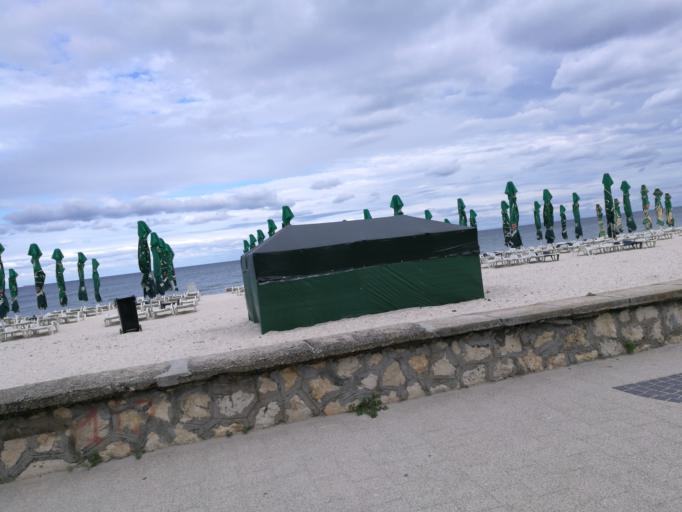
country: RO
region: Constanta
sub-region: Municipiul Constanta
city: Palazu Mare
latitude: 44.2532
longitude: 28.6217
